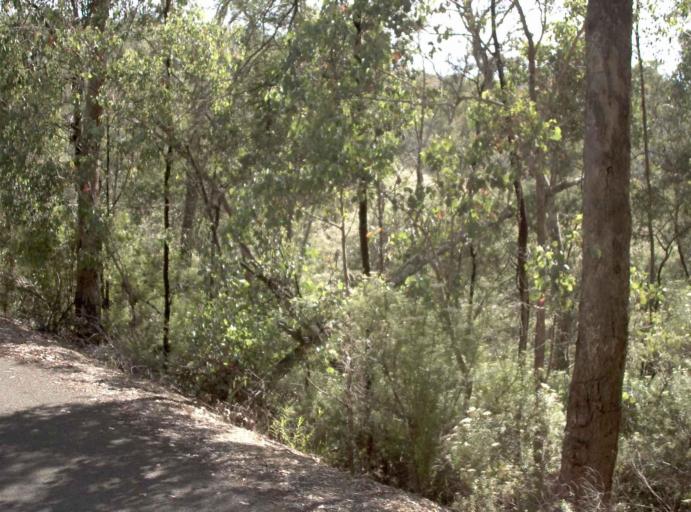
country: AU
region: Victoria
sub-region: East Gippsland
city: Lakes Entrance
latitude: -37.4683
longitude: 148.1245
